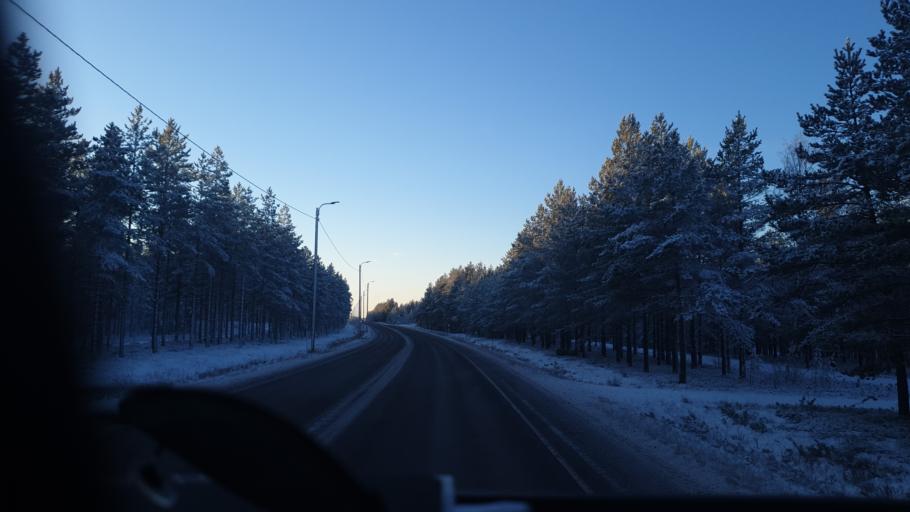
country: FI
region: Northern Ostrobothnia
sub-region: Ylivieska
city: Kalajoki
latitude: 64.2383
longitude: 23.8363
